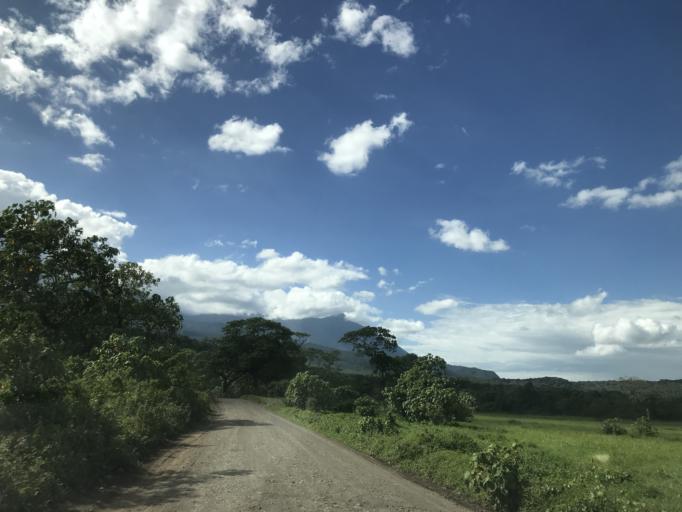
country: TZ
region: Arusha
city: Usa River
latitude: -3.3050
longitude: 36.8753
